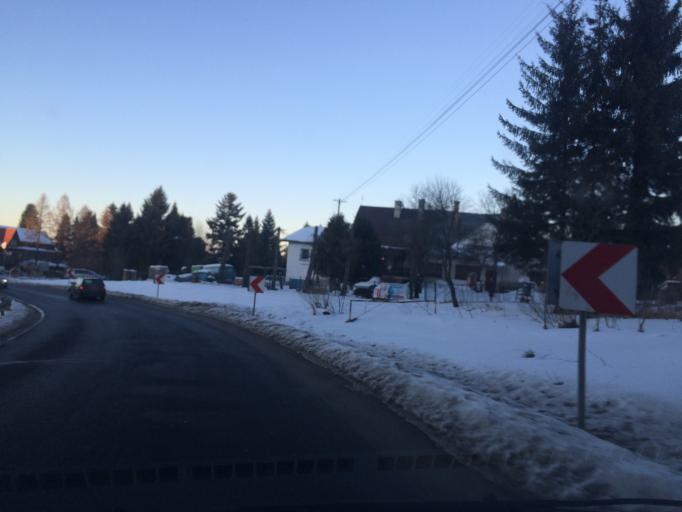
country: PL
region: Subcarpathian Voivodeship
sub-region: Powiat bieszczadzki
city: Czarna
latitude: 49.3076
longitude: 22.6727
